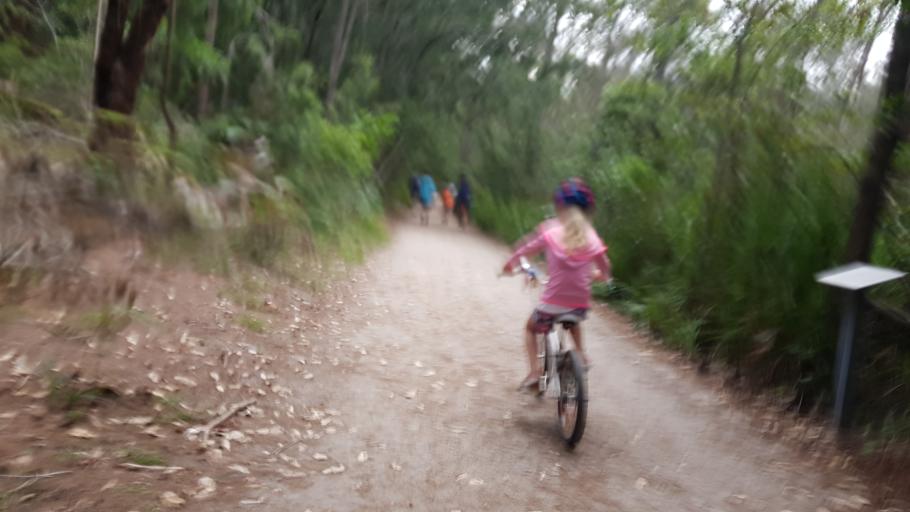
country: AU
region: New South Wales
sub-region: Warringah
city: Narrabeen
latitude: -33.7195
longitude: 151.2789
